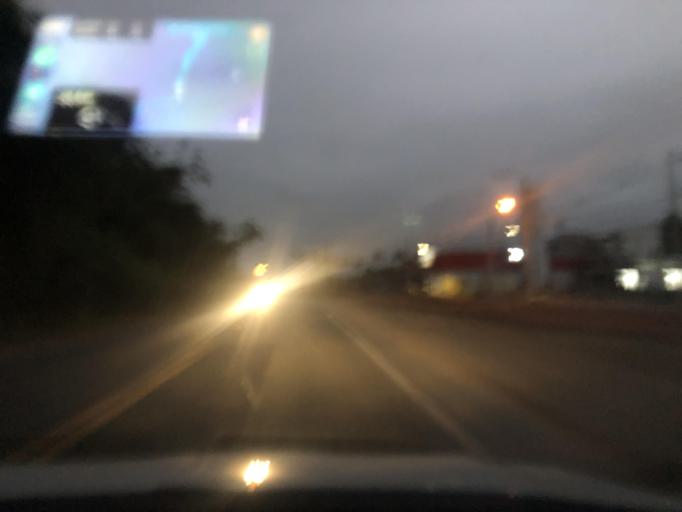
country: BR
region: Santa Catarina
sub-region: Guaramirim
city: Guaramirim
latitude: -26.5899
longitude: -48.9879
